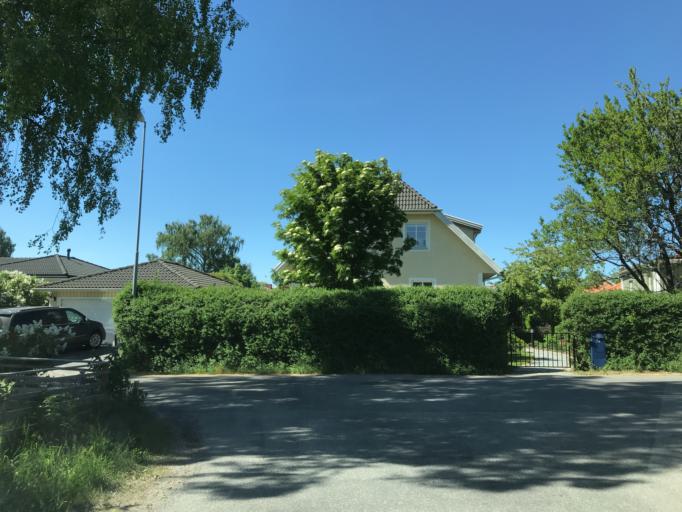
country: SE
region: Stockholm
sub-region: Sollentuna Kommun
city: Sollentuna
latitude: 59.4228
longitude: 17.9598
